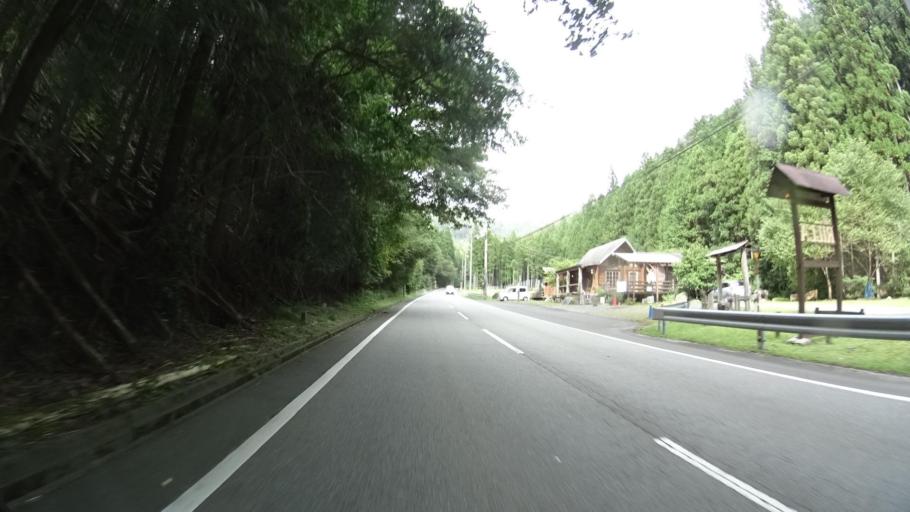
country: JP
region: Kyoto
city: Kameoka
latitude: 35.2161
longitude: 135.5693
